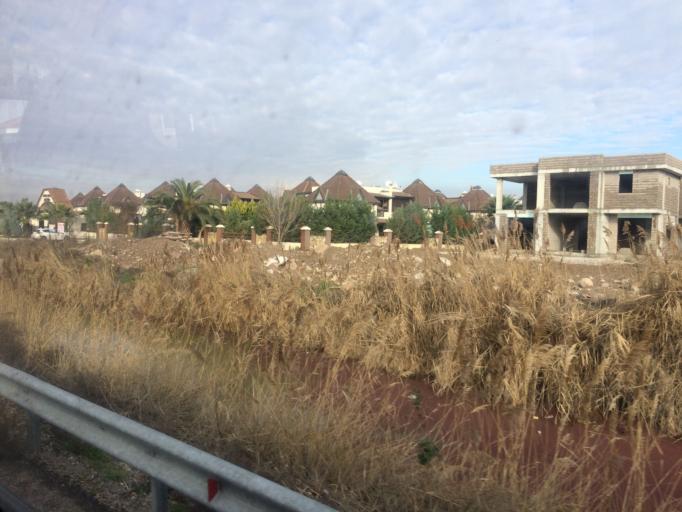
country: TR
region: Izmir
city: Menemen
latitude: 38.5061
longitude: 26.9586
